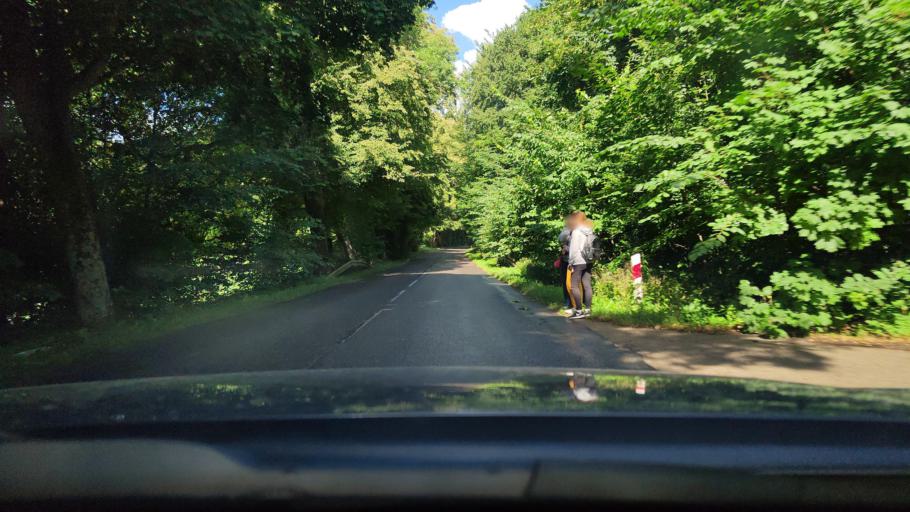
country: PL
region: Pomeranian Voivodeship
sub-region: Powiat pucki
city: Krokowa
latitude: 54.7338
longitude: 18.1632
